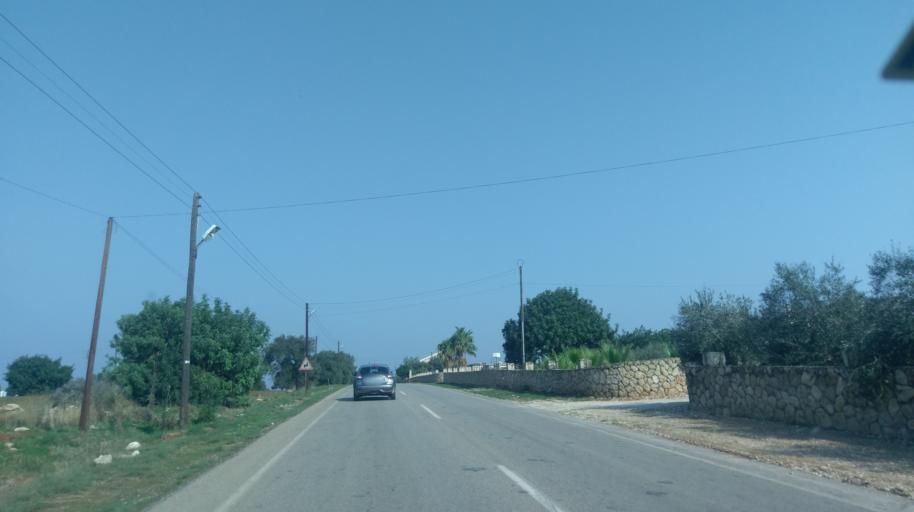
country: CY
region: Ammochostos
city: Leonarisso
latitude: 35.5229
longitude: 34.1756
